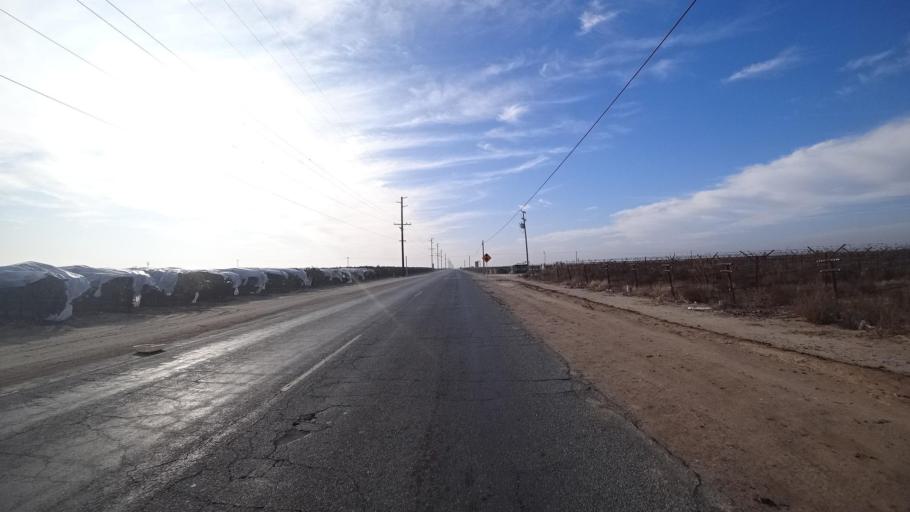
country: US
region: California
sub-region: Kern County
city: Delano
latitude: 35.7494
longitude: -119.2053
